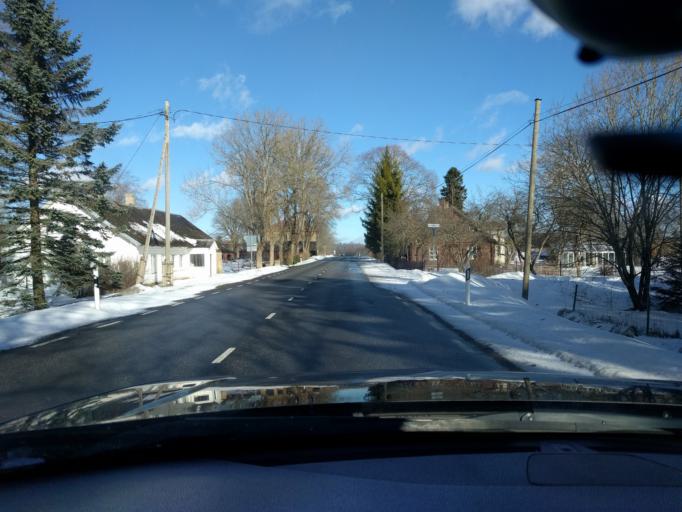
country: EE
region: Harju
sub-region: Raasiku vald
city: Raasiku
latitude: 59.3796
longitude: 25.1948
